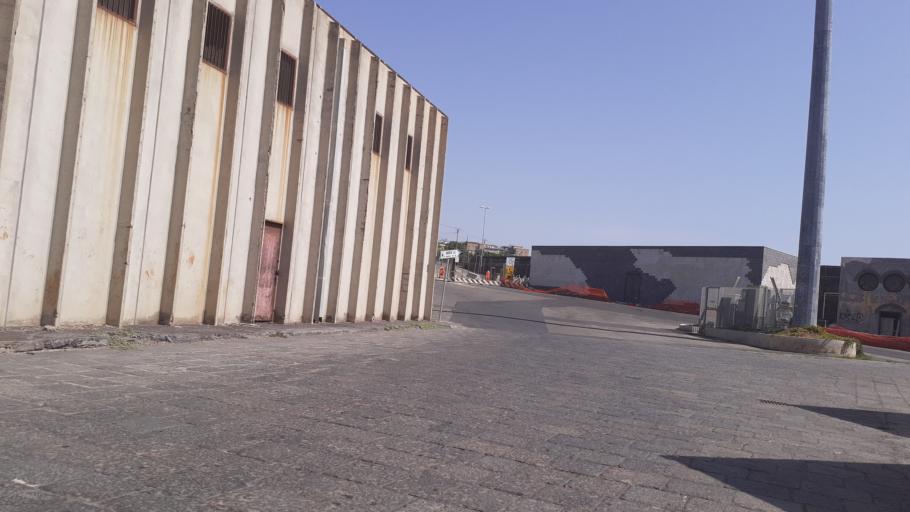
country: IT
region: Sicily
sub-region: Catania
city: Catania
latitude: 37.5021
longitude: 15.0963
